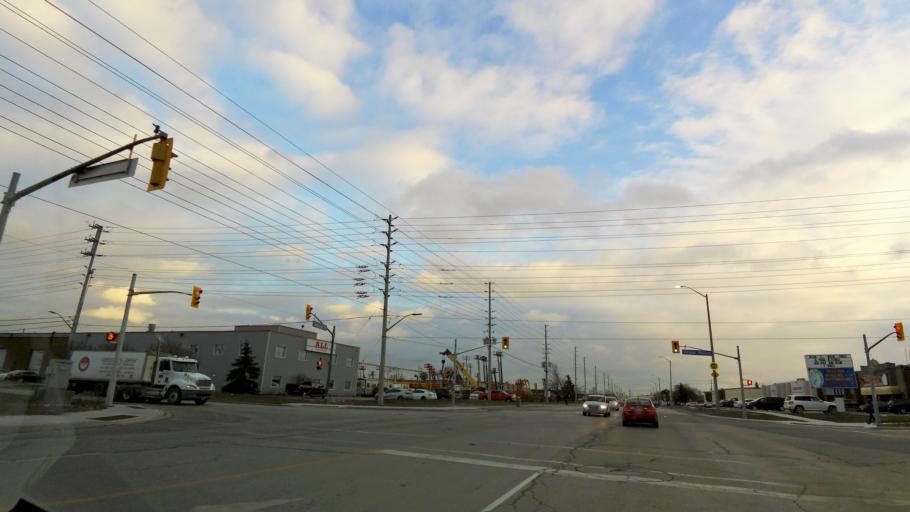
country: CA
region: Ontario
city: Etobicoke
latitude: 43.6994
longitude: -79.6598
